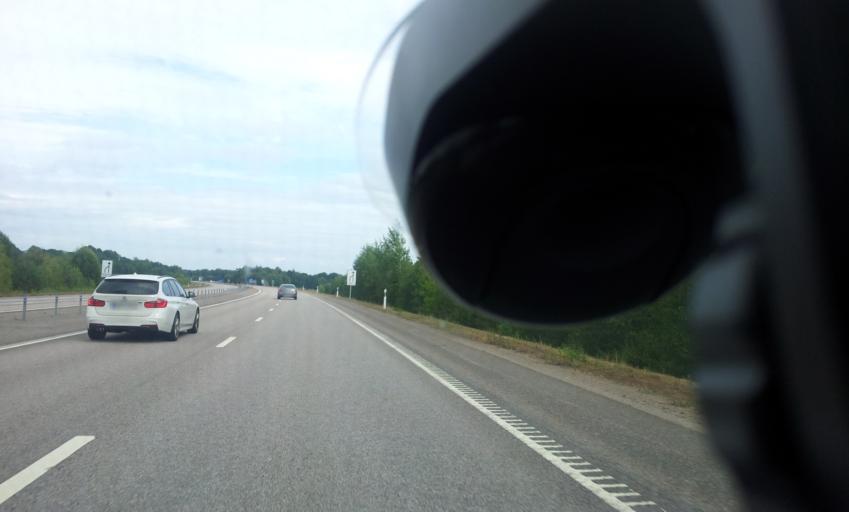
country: SE
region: Kalmar
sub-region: Kalmar Kommun
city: Ljungbyholm
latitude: 56.6317
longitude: 16.2032
